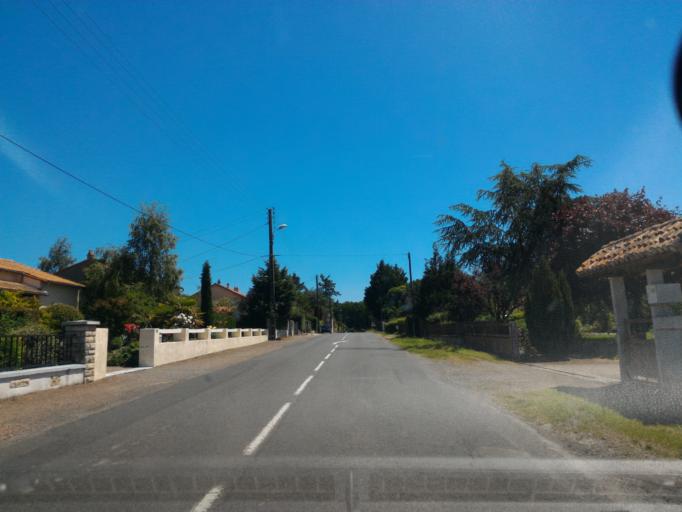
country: FR
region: Poitou-Charentes
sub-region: Departement de la Vienne
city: Availles-Limouzine
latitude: 46.2272
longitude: 0.6891
